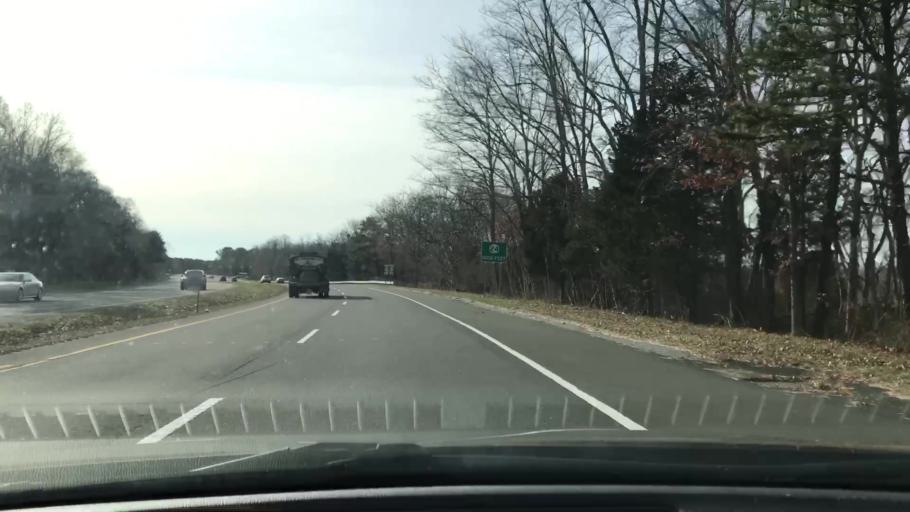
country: US
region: New York
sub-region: Suffolk County
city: Riverhead
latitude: 40.9148
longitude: -72.6410
